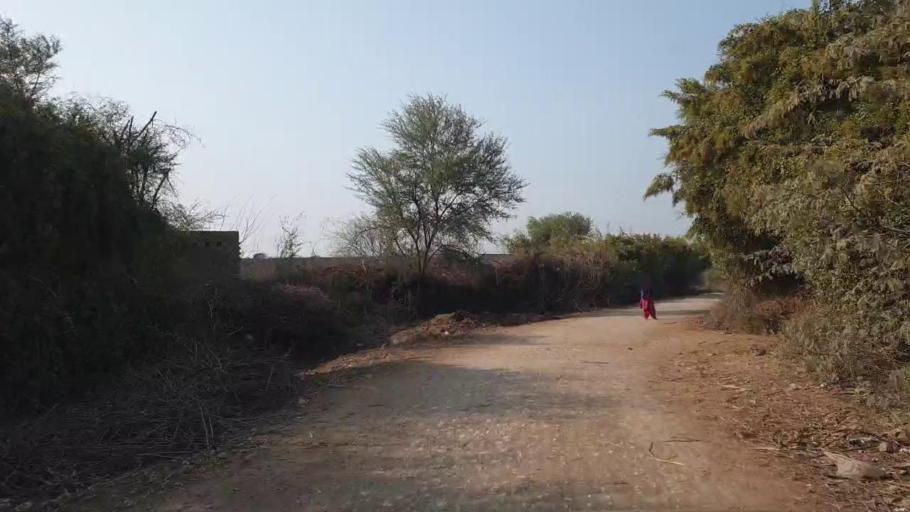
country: PK
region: Sindh
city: Bhit Shah
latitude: 25.8962
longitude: 68.4718
